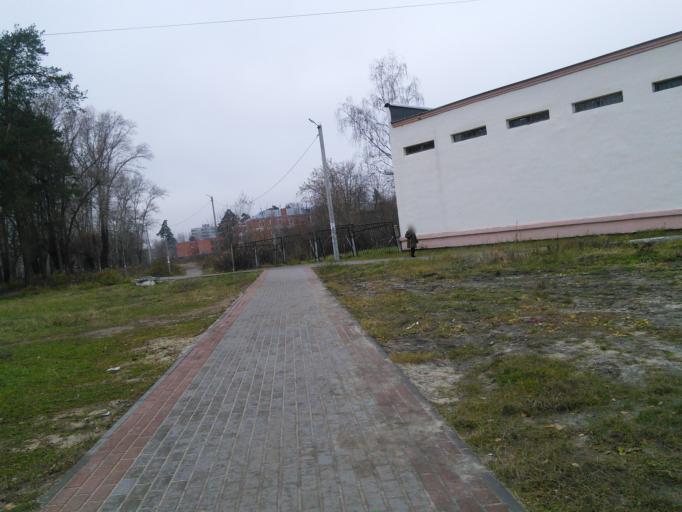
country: RU
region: Moskovskaya
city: Likino-Dulevo
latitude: 55.7149
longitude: 38.9571
